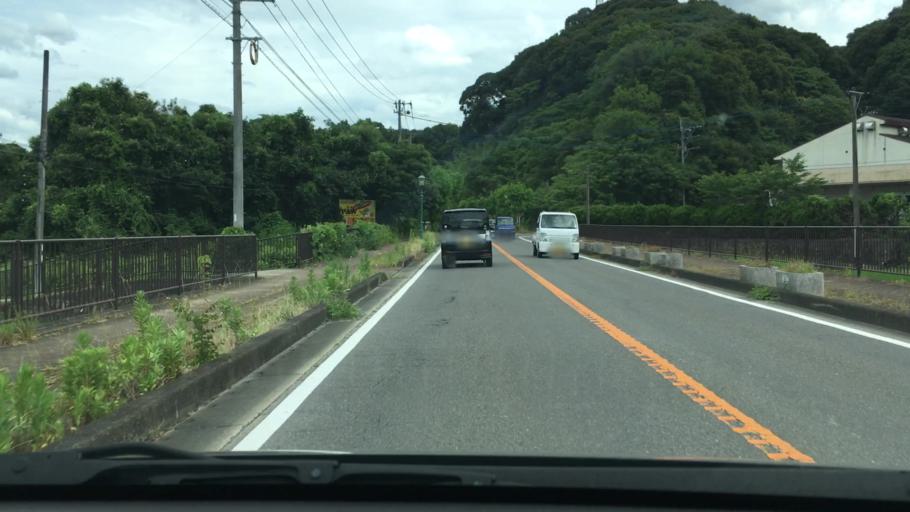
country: JP
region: Nagasaki
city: Togitsu
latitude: 32.9880
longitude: 129.7668
